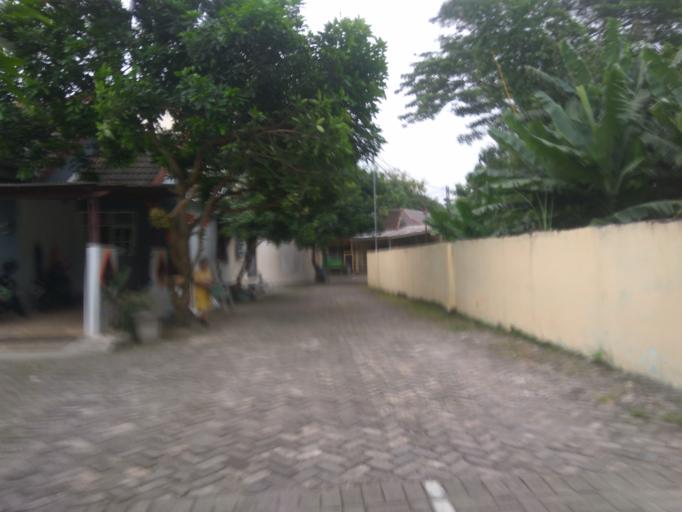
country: ID
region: Central Java
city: Mranggen
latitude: -7.0251
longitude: 110.4651
